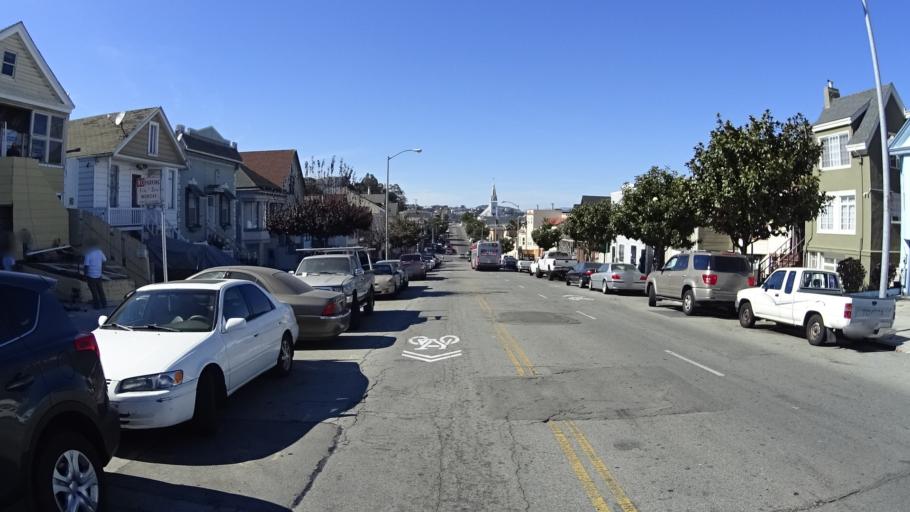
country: US
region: California
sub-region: San Francisco County
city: San Francisco
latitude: 37.7331
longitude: -122.3894
